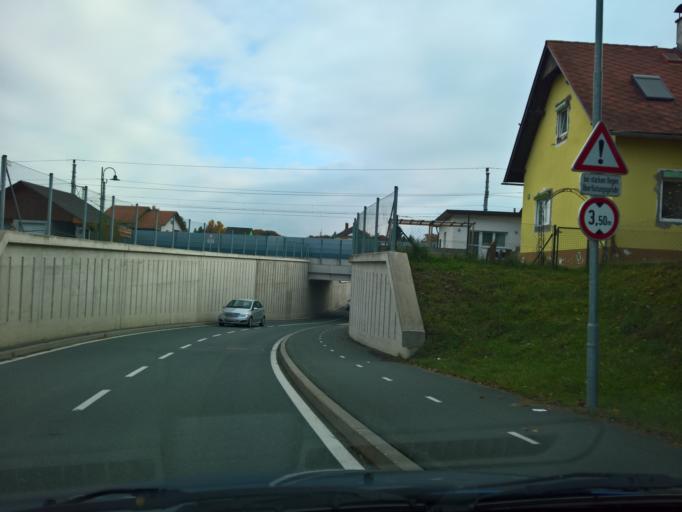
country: AT
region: Styria
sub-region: Politischer Bezirk Leibnitz
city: Kaindorf an der Sulm
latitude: 46.7901
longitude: 15.5443
